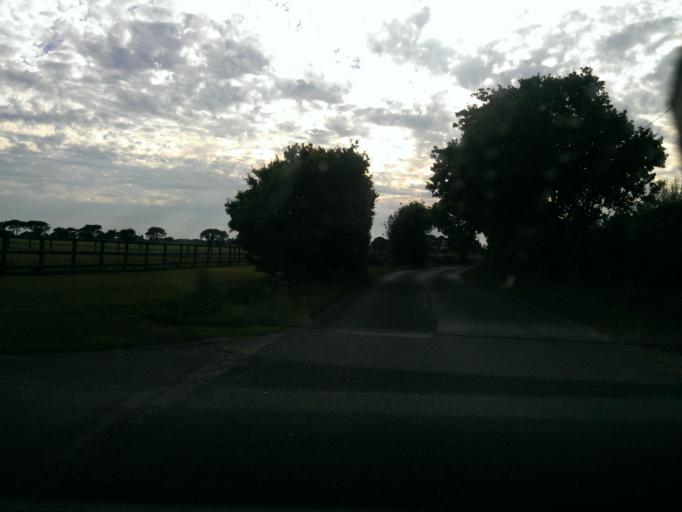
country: GB
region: England
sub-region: Essex
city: Great Bentley
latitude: 51.8397
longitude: 1.0950
